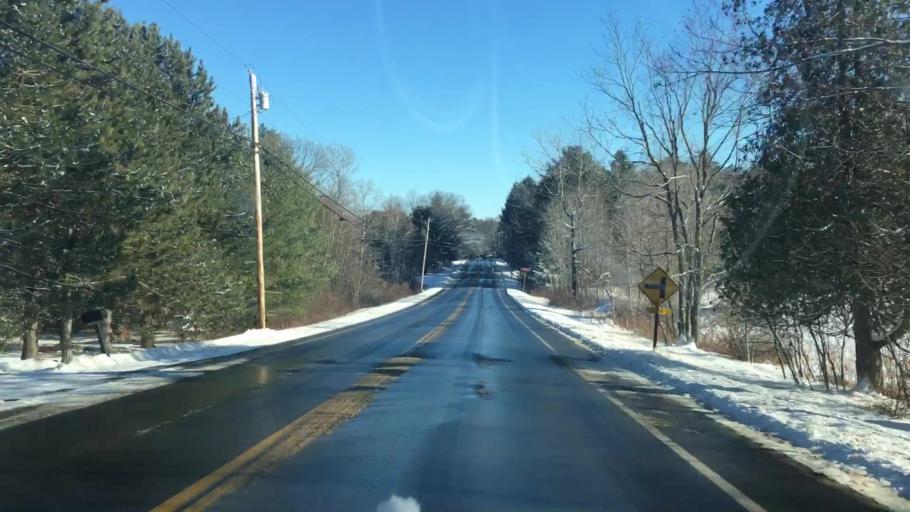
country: US
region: Maine
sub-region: Sagadahoc County
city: Topsham
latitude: 43.9142
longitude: -70.0257
